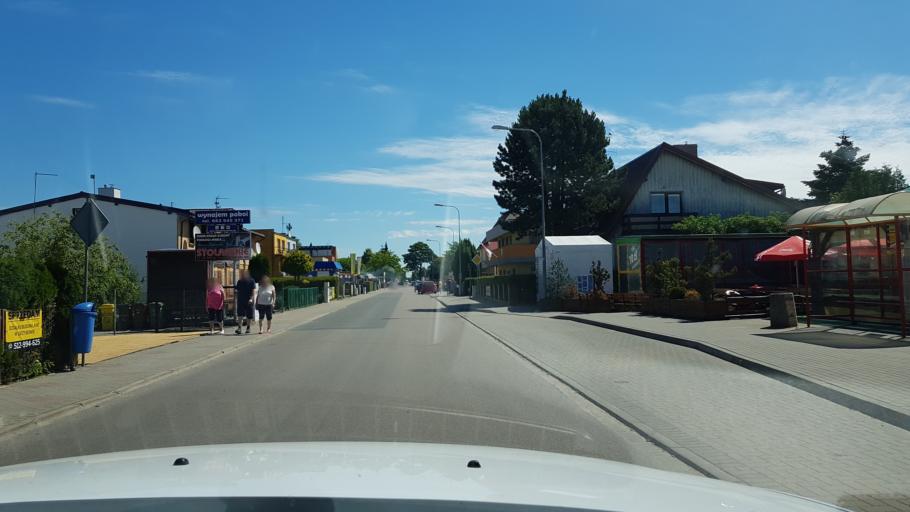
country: PL
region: West Pomeranian Voivodeship
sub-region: Powiat kolobrzeski
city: Grzybowo
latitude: 54.1629
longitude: 15.4940
